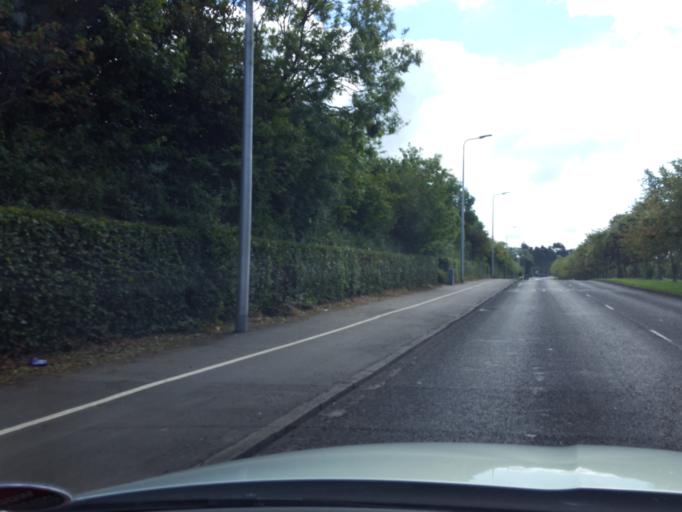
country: GB
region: Scotland
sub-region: Fife
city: Rosyth
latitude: 56.0558
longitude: -3.4389
